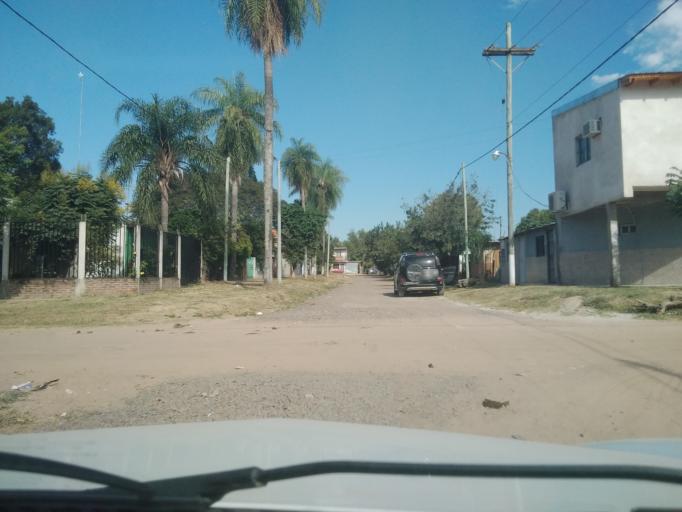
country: AR
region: Corrientes
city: Corrientes
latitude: -27.5091
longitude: -58.8052
